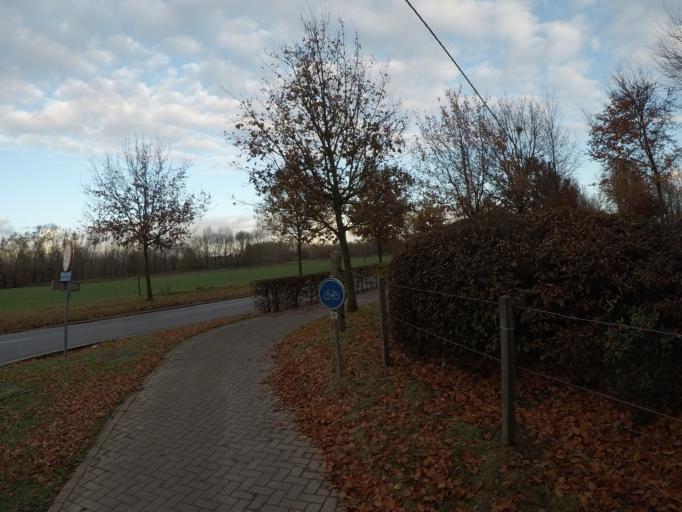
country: BE
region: Flanders
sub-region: Provincie Vlaams-Brabant
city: Londerzeel
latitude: 51.0020
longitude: 4.2680
